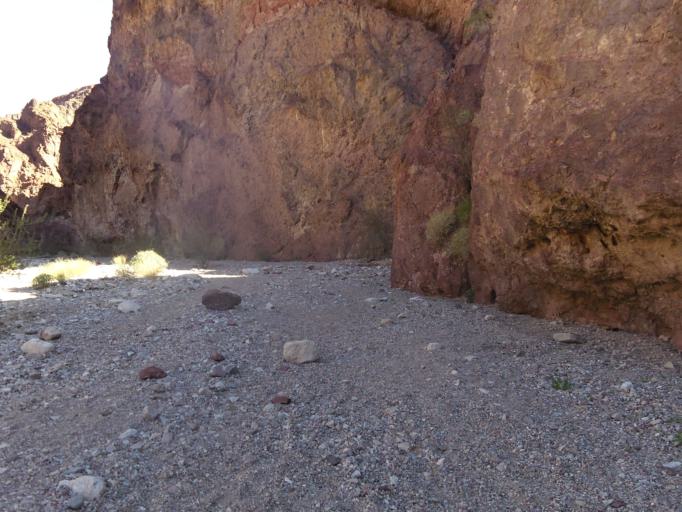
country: US
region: Nevada
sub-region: Clark County
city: Boulder City
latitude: 35.9634
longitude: -114.7289
